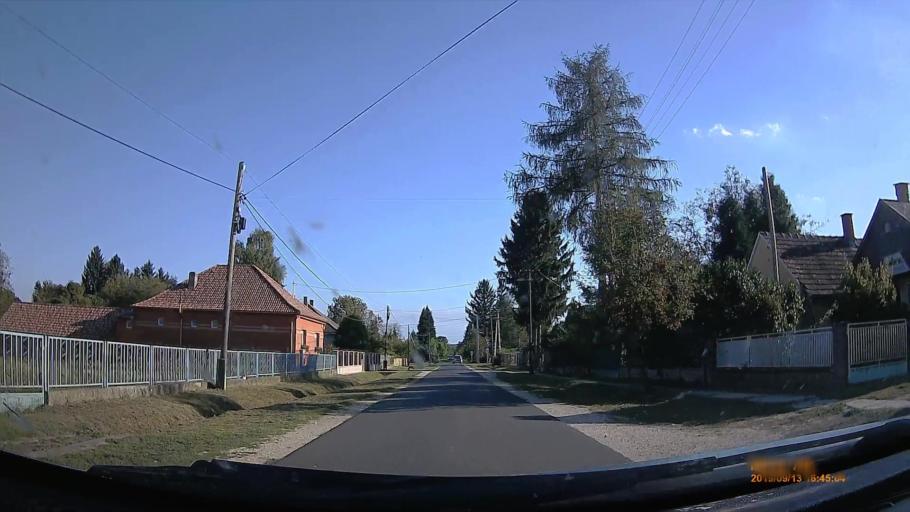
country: HU
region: Zala
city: Pacsa
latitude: 46.6267
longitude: 17.0573
